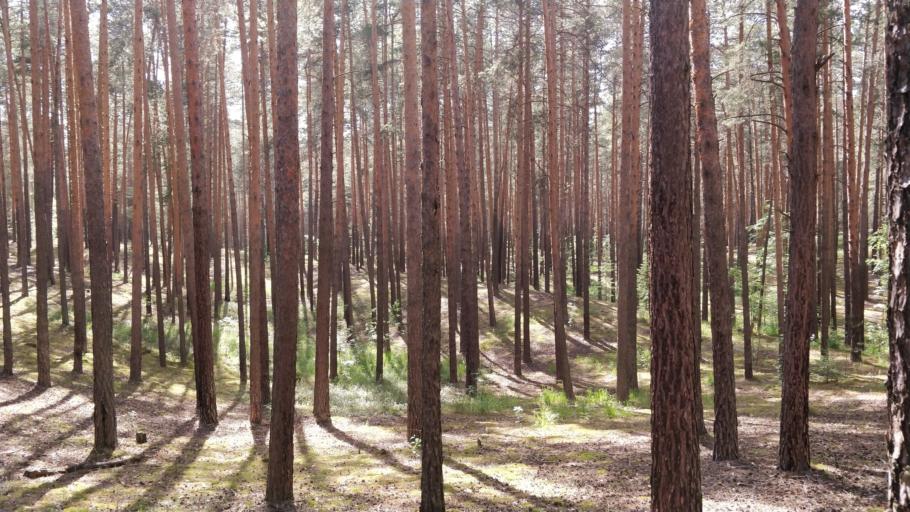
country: RU
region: Perm
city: Perm
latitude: 58.0726
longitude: 56.3033
